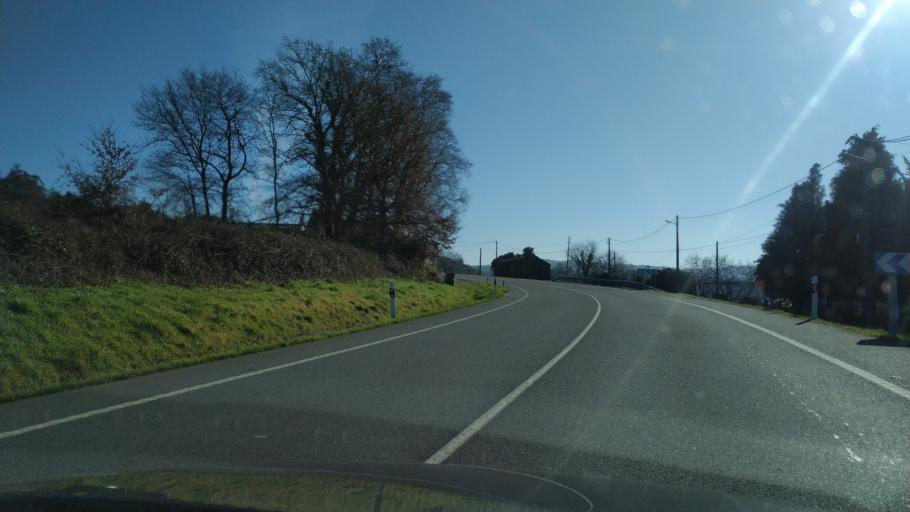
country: ES
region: Galicia
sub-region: Provincia da Coruna
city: Ribeira
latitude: 42.7534
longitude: -8.3858
